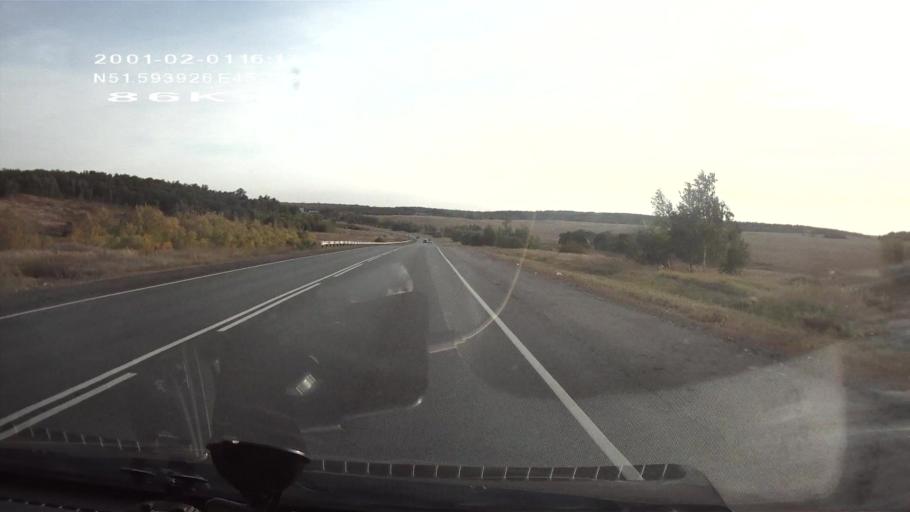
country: RU
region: Saratov
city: Sokolovyy
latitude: 51.5933
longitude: 45.7694
